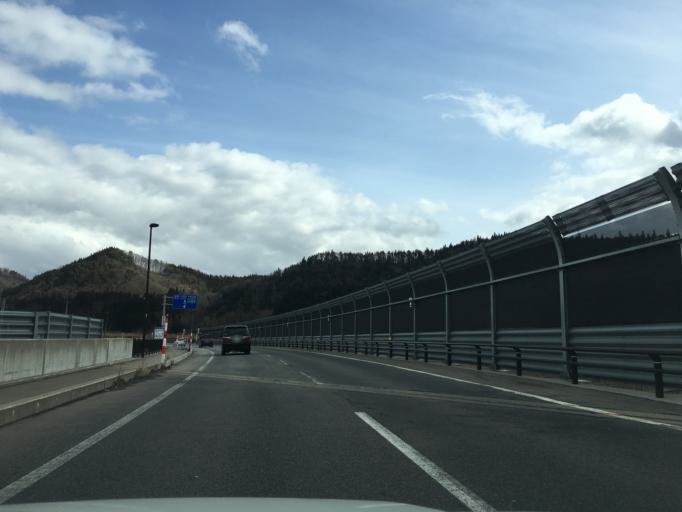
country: JP
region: Akita
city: Hanawa
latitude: 40.2240
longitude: 140.7172
